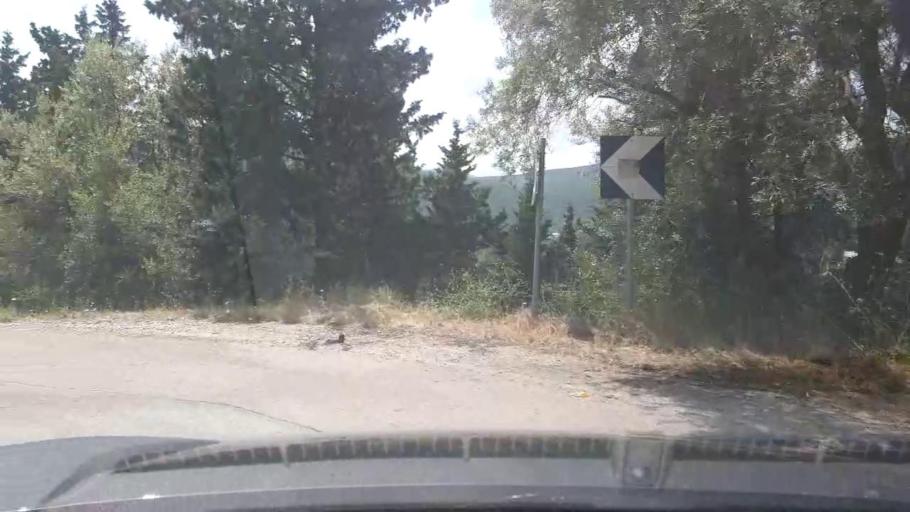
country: GR
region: Ionian Islands
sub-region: Lefkada
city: Nidri
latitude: 38.6491
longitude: 20.7036
